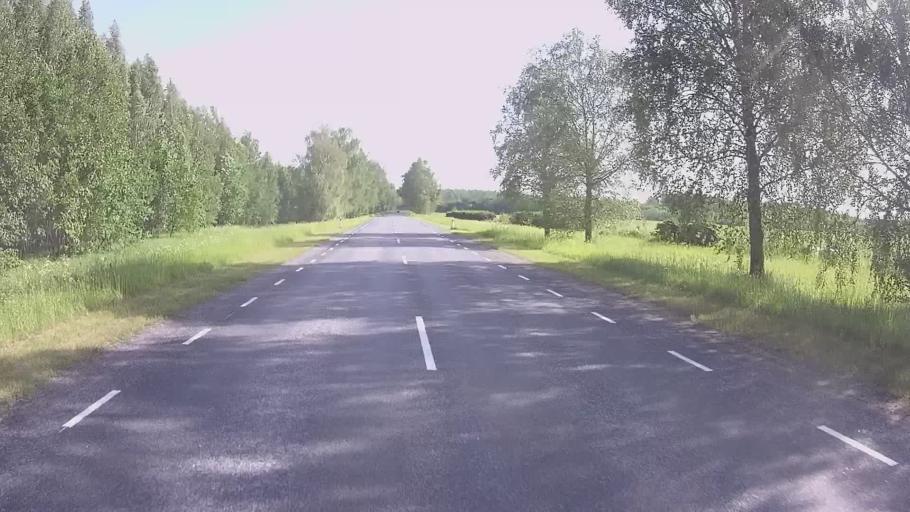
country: EE
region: Valgamaa
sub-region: Torva linn
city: Torva
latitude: 58.0687
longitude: 26.0323
